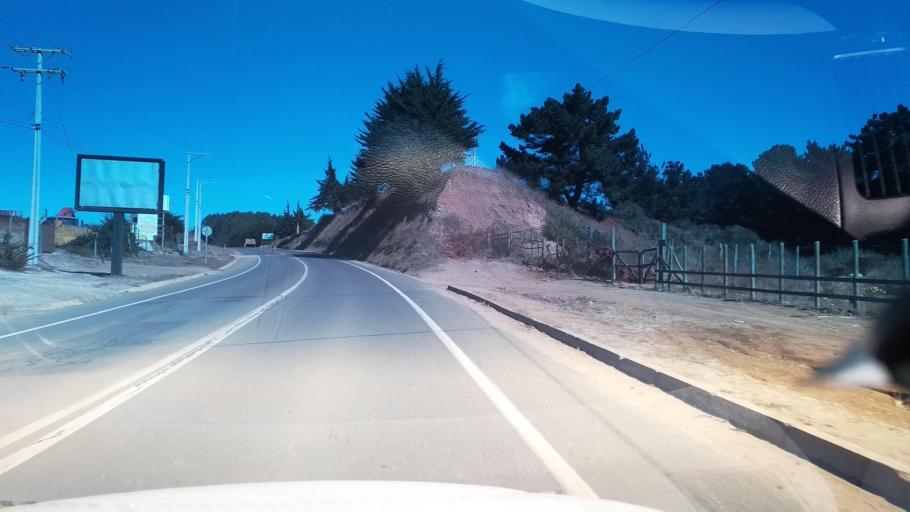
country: CL
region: O'Higgins
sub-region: Provincia de Colchagua
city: Santa Cruz
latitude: -34.4311
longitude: -72.0336
